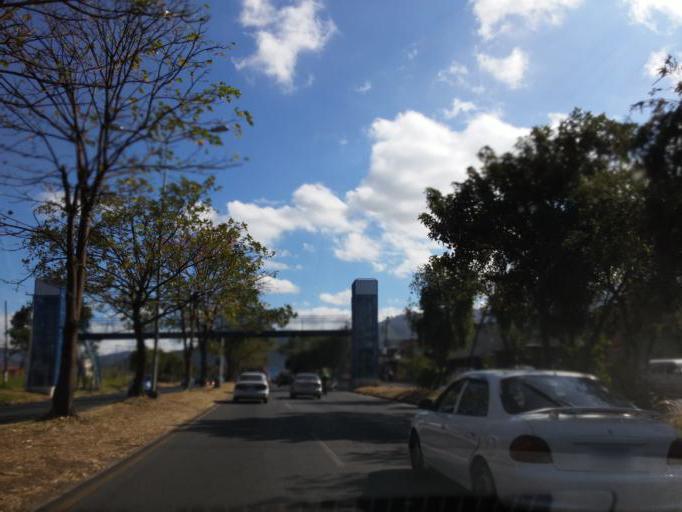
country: CR
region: San Jose
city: San Felipe
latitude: 9.9162
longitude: -84.1061
